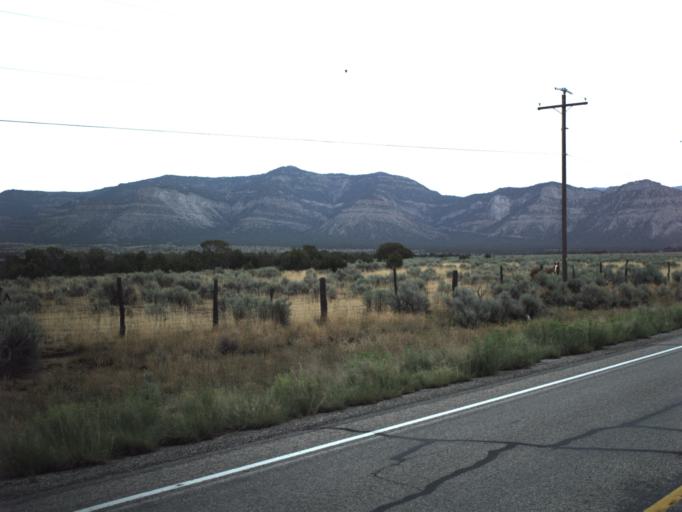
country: US
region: Utah
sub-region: Carbon County
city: East Carbon City
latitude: 39.5376
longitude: -110.4503
